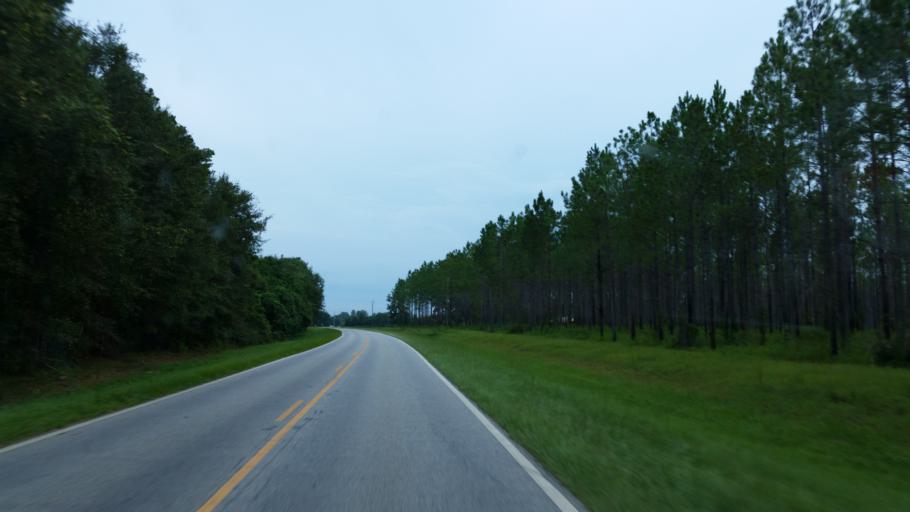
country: US
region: Georgia
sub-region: Lowndes County
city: Valdosta
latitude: 30.7466
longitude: -83.3107
